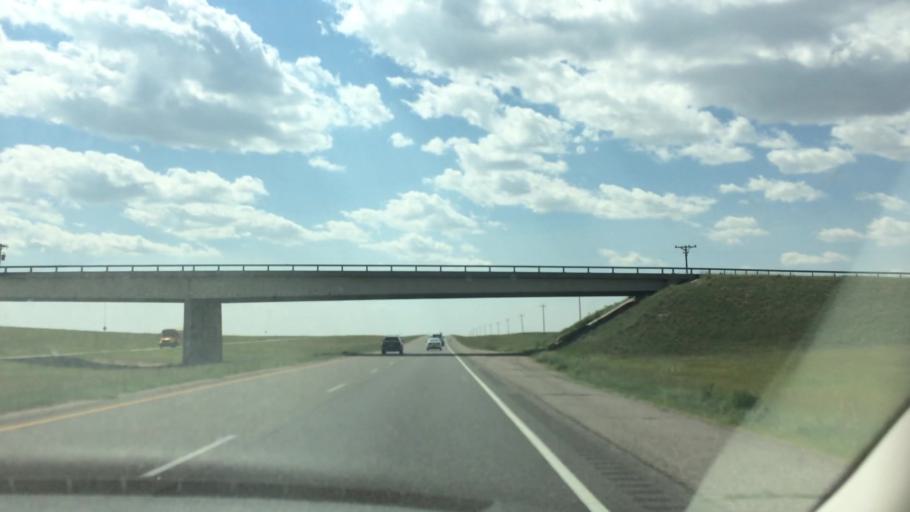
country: US
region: Colorado
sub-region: Lincoln County
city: Hugo
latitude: 39.2877
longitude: -103.0984
